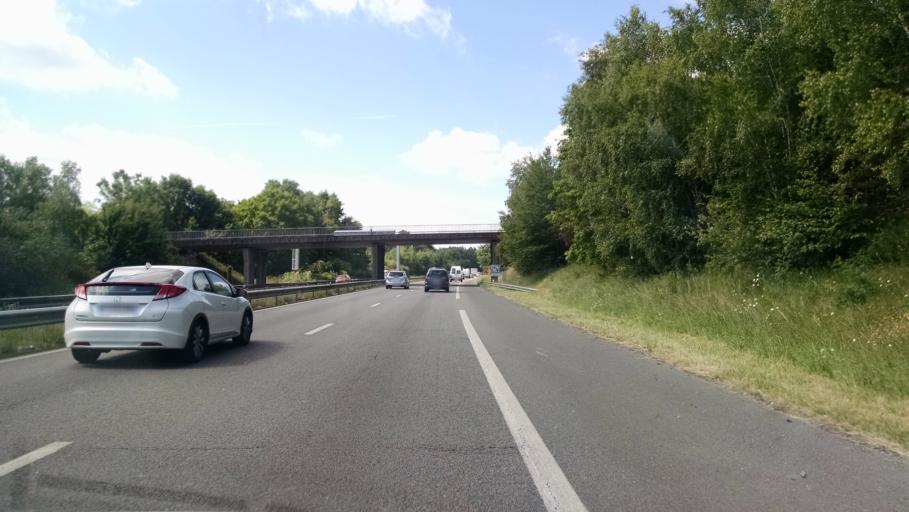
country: FR
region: Pays de la Loire
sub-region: Departement de la Loire-Atlantique
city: Les Sorinieres
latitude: 47.1671
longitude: -1.5219
